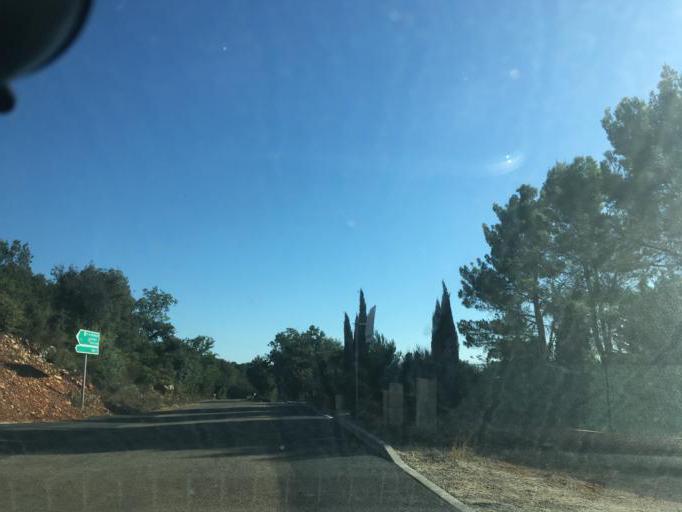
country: FR
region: Provence-Alpes-Cote d'Azur
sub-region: Departement du Var
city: Regusse
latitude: 43.7142
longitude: 6.1404
